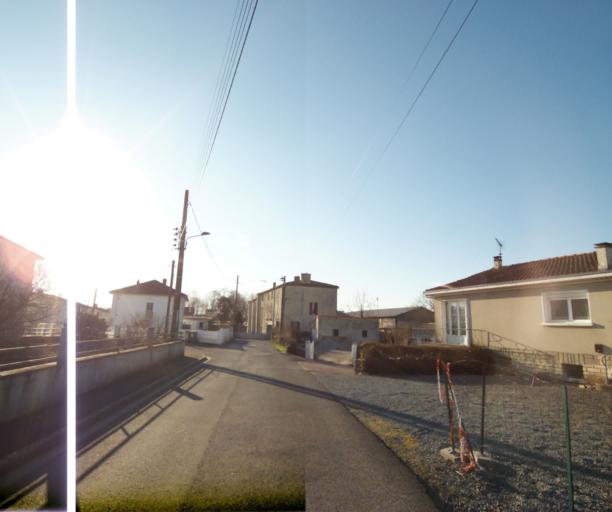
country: FR
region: Poitou-Charentes
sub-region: Departement des Deux-Sevres
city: Niort
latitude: 46.3337
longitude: -0.4743
